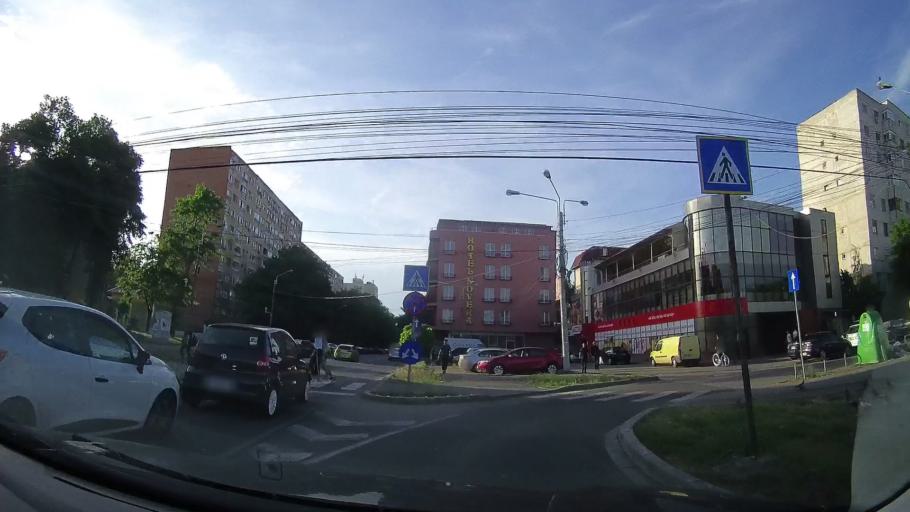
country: RO
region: Timis
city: Timisoara
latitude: 45.7429
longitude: 21.2431
